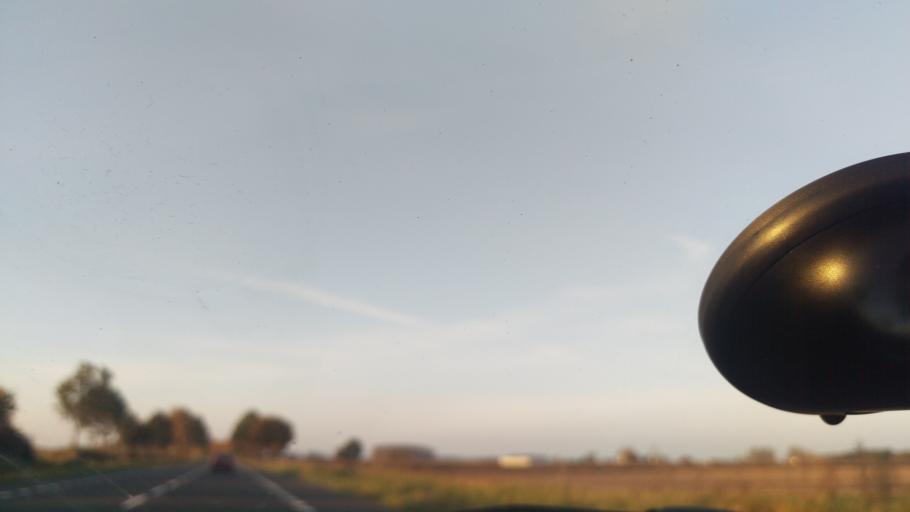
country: PL
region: West Pomeranian Voivodeship
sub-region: Powiat gryfinski
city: Stare Czarnowo
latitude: 53.2251
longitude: 14.7951
